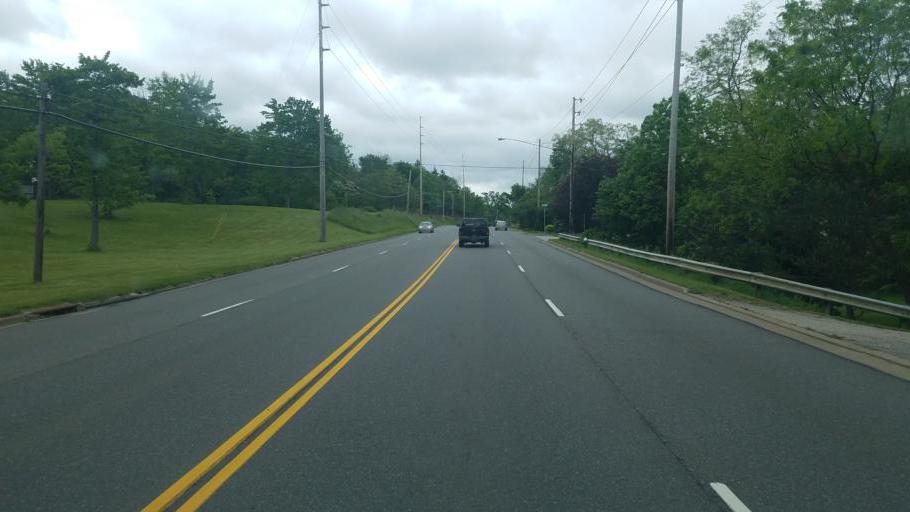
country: US
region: Ohio
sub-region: Summit County
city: Reminderville
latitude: 41.3447
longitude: -81.3734
